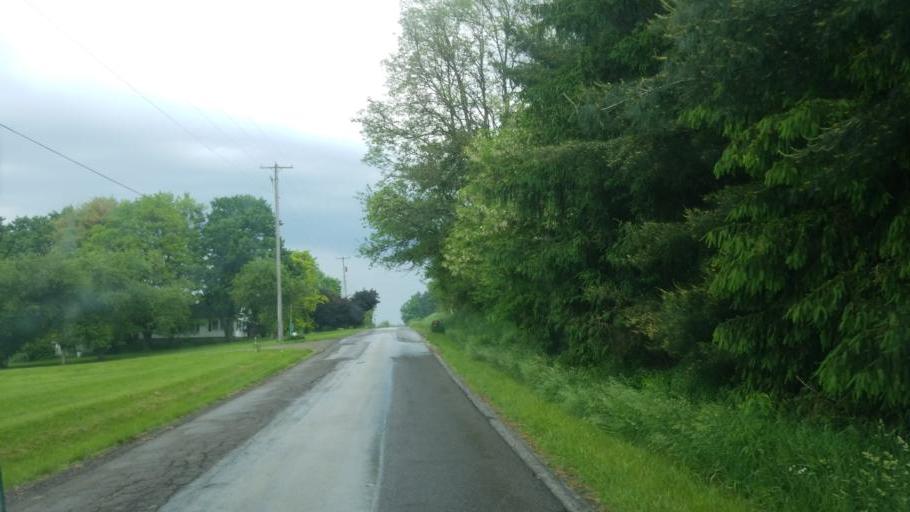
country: US
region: Ohio
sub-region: Wayne County
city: Dalton
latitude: 40.7667
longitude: -81.7067
